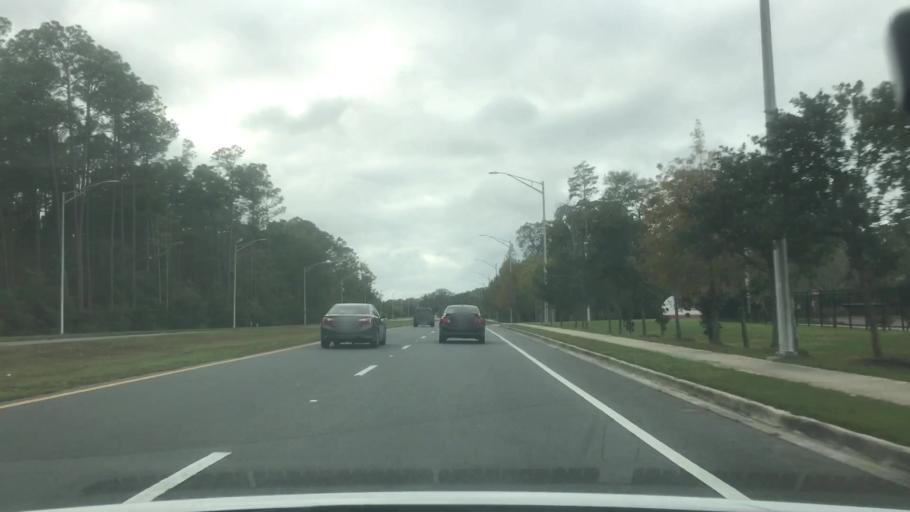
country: US
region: Florida
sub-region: Duval County
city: Jacksonville
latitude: 30.4761
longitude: -81.6175
